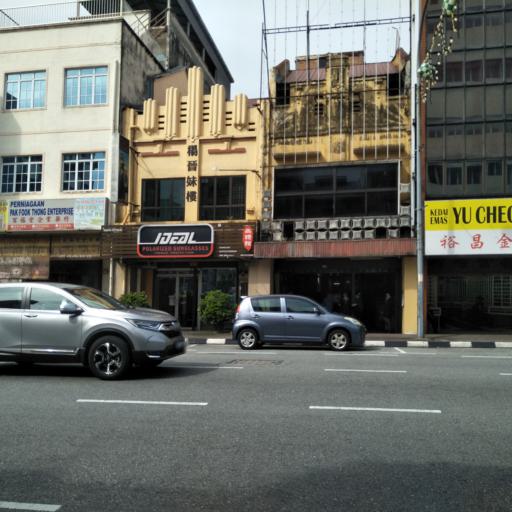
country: MY
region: Perak
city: Ipoh
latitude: 4.5939
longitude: 101.0819
